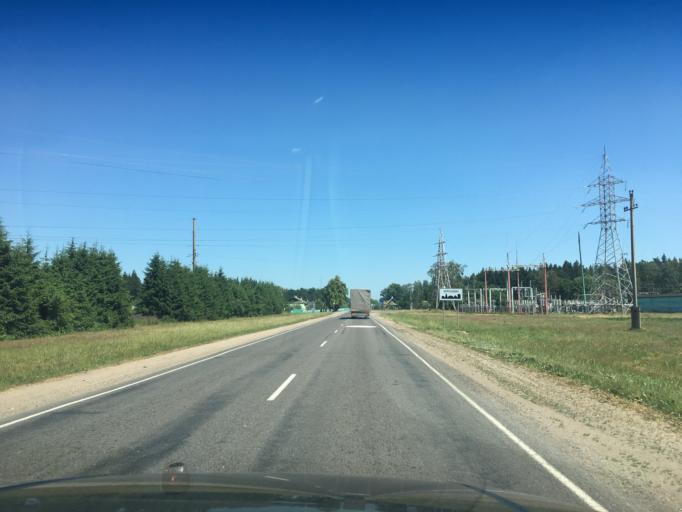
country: BY
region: Grodnenskaya
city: Iwye
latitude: 54.0244
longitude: 25.9176
